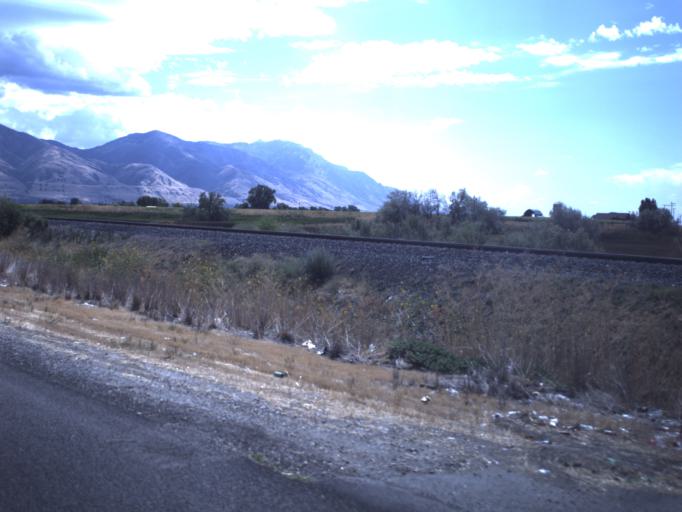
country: US
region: Utah
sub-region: Box Elder County
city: Brigham City
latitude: 41.5446
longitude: -112.0937
